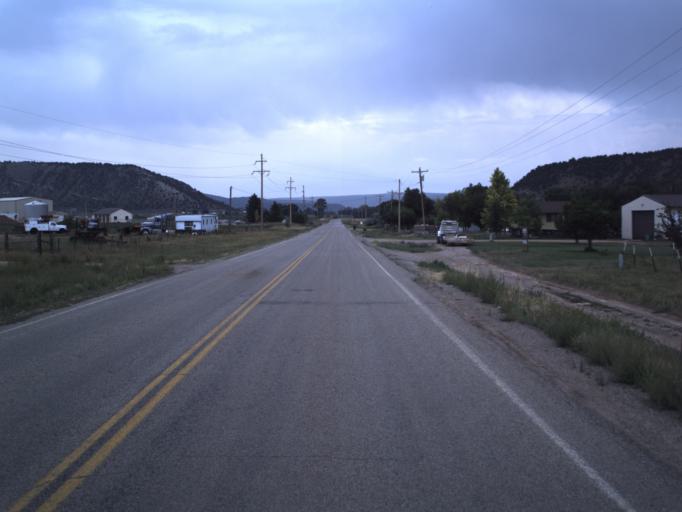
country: US
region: Utah
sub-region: Duchesne County
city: Duchesne
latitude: 40.4031
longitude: -110.7638
